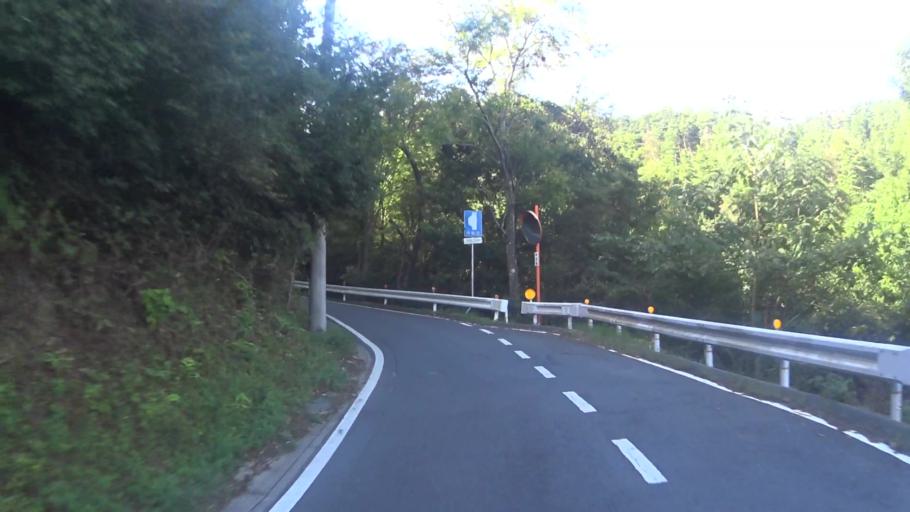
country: JP
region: Kyoto
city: Uji
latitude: 34.8099
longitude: 135.8920
